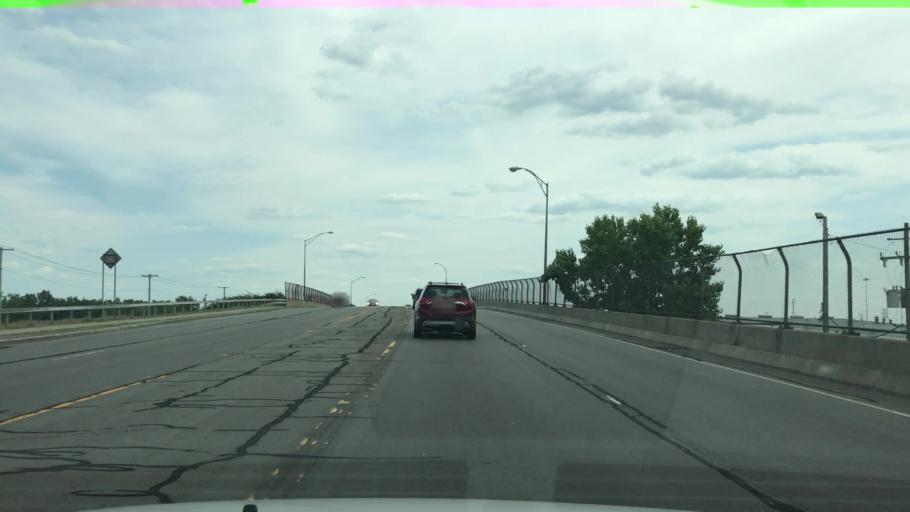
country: US
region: New York
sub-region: Erie County
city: Sloan
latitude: 42.8932
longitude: -78.7846
